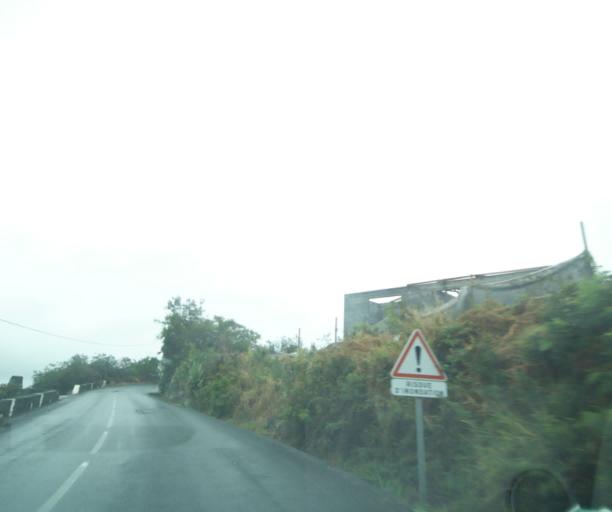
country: RE
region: Reunion
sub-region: Reunion
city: Saint-Paul
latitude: -21.0227
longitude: 55.2942
